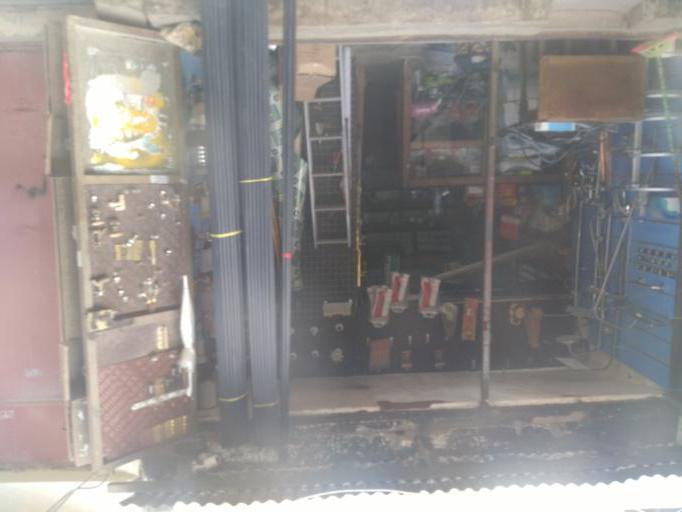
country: TZ
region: Zanzibar Urban/West
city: Zanzibar
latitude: -6.1609
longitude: 39.2009
